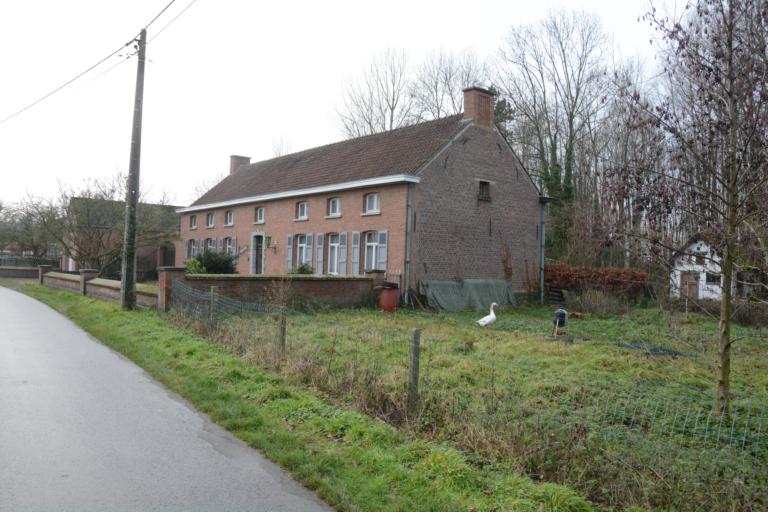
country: BE
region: Flanders
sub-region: Provincie Vlaams-Brabant
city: Merchtem
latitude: 50.9824
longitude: 4.2599
